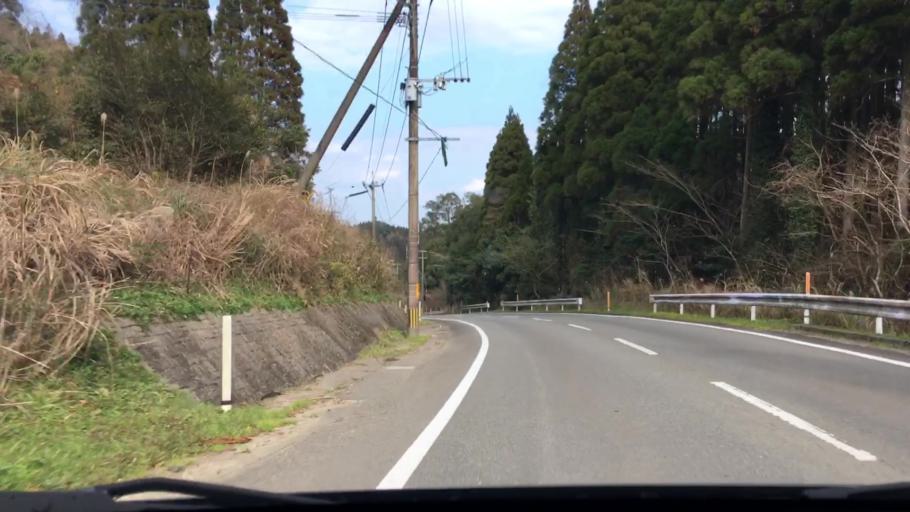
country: JP
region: Miyazaki
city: Kushima
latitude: 31.5772
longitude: 131.2704
